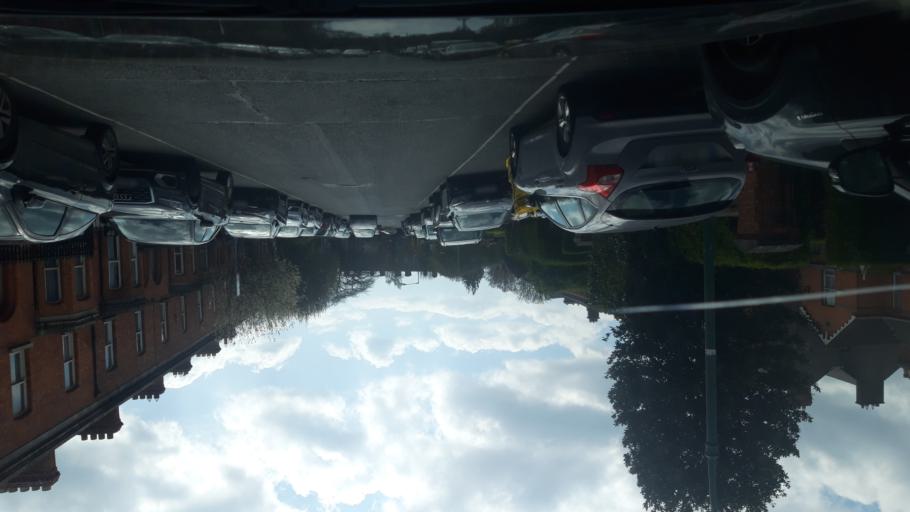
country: IE
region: Leinster
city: Rathgar
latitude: 53.3212
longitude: -6.2723
